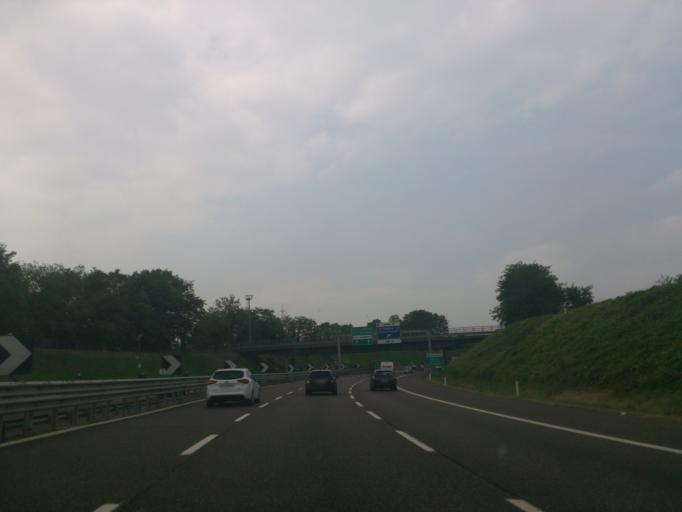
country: IT
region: Lombardy
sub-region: Provincia di Monza e Brianza
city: Brugherio
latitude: 45.5402
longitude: 9.3148
